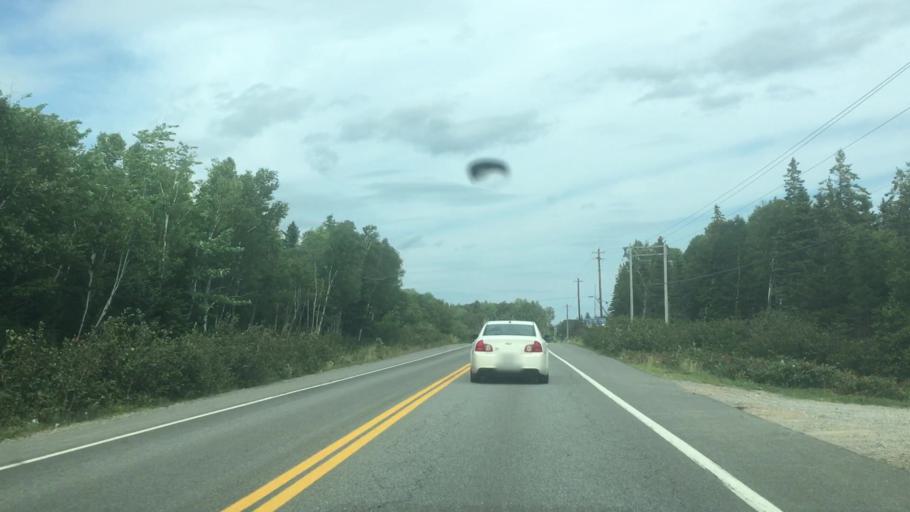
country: CA
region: Nova Scotia
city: Sydney Mines
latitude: 46.5200
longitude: -60.4232
